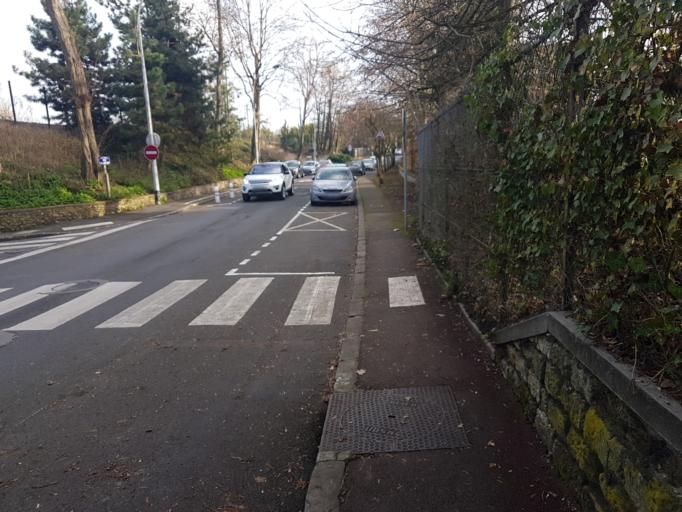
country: FR
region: Ile-de-France
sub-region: Departement des Yvelines
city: Louveciennes
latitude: 48.8637
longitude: 2.1161
